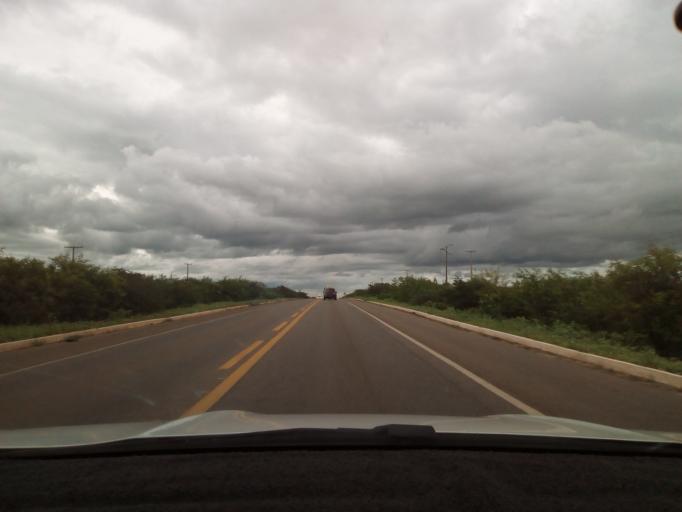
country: BR
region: Rio Grande do Norte
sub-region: Mossoro
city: Mossoro
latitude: -4.9609
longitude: -37.3960
